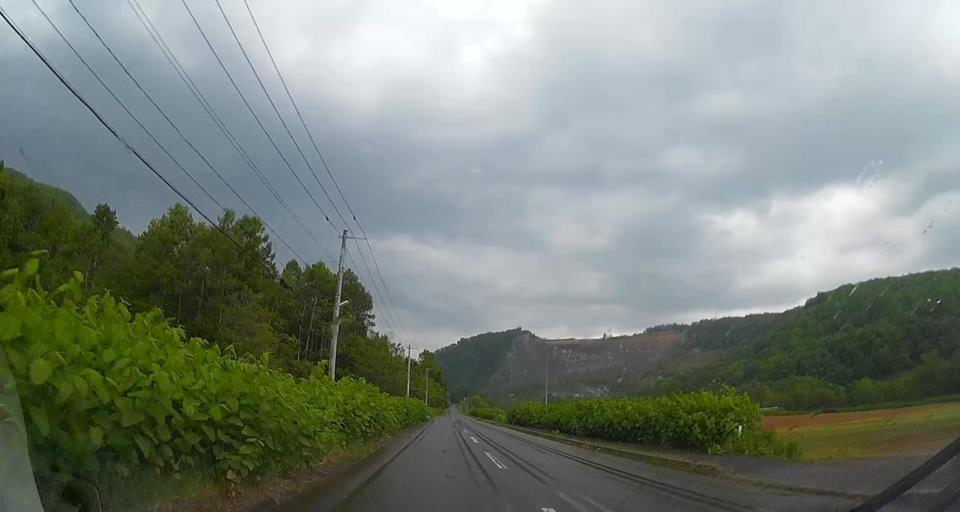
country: JP
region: Hokkaido
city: Niseko Town
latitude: 42.8950
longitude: 140.9026
